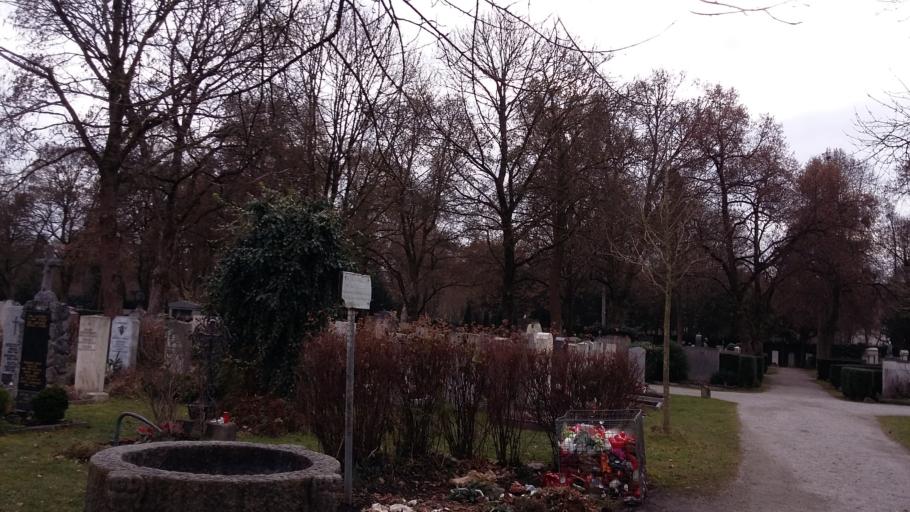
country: DE
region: Bavaria
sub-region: Upper Bavaria
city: Pasing
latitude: 48.1369
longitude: 11.4583
